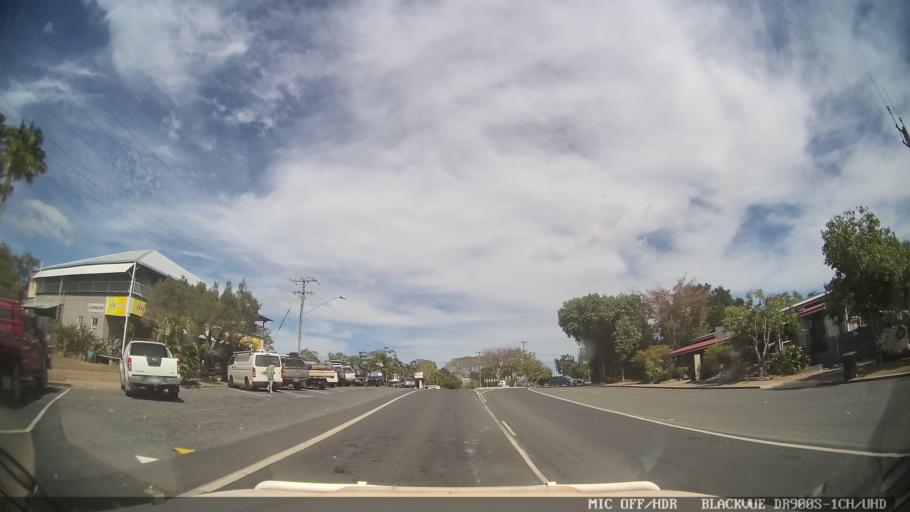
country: AU
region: Queensland
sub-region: Cairns
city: Port Douglas
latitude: -16.6734
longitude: 145.3297
